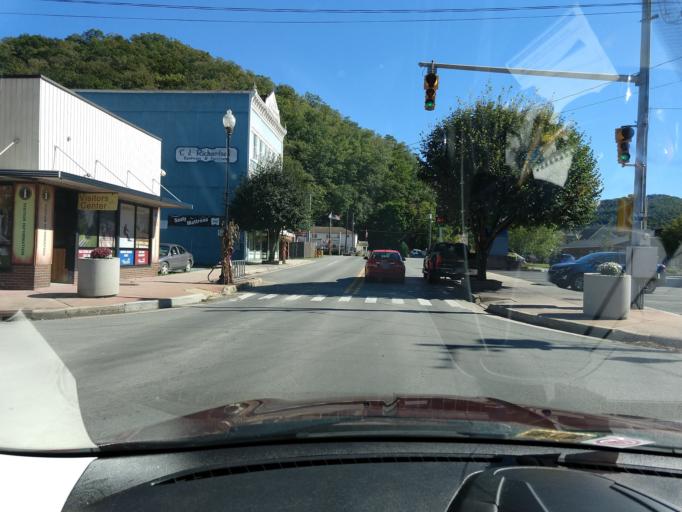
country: US
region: West Virginia
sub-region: Pocahontas County
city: Marlinton
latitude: 38.2230
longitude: -80.0937
